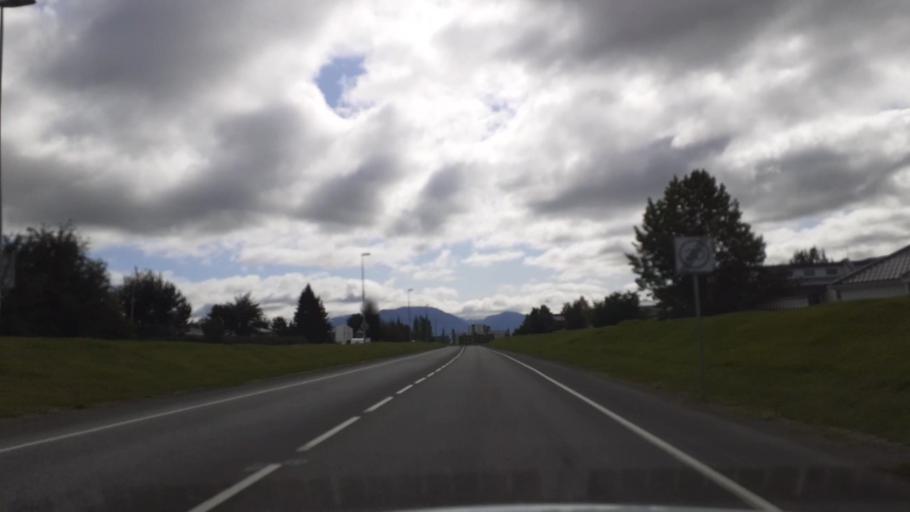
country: IS
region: Northeast
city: Akureyri
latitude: 65.6736
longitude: -18.1091
